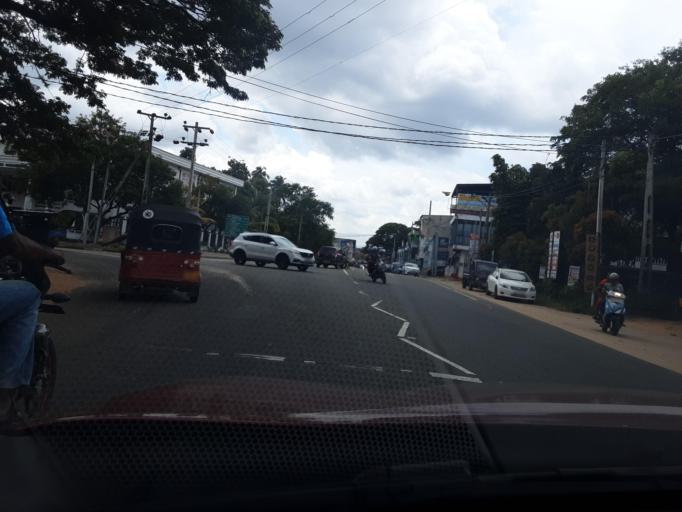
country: LK
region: North Western
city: Kurunegala
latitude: 7.4329
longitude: 80.2127
